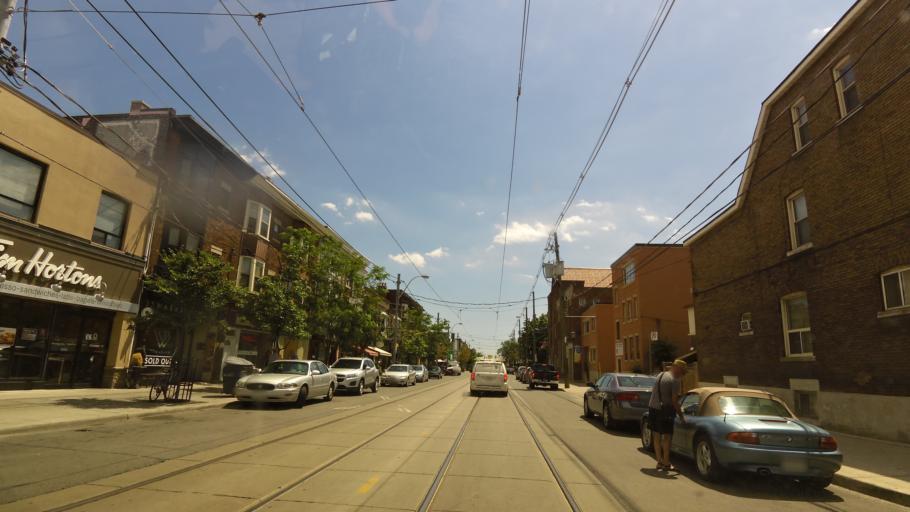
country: CA
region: Ontario
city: Toronto
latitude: 43.6445
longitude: -79.4484
